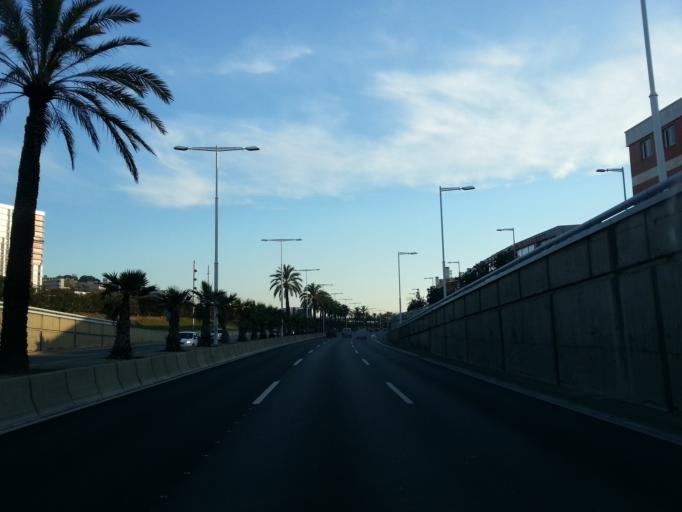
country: ES
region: Catalonia
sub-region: Provincia de Barcelona
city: Santa Coloma de Gramenet
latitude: 41.4430
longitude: 2.2065
